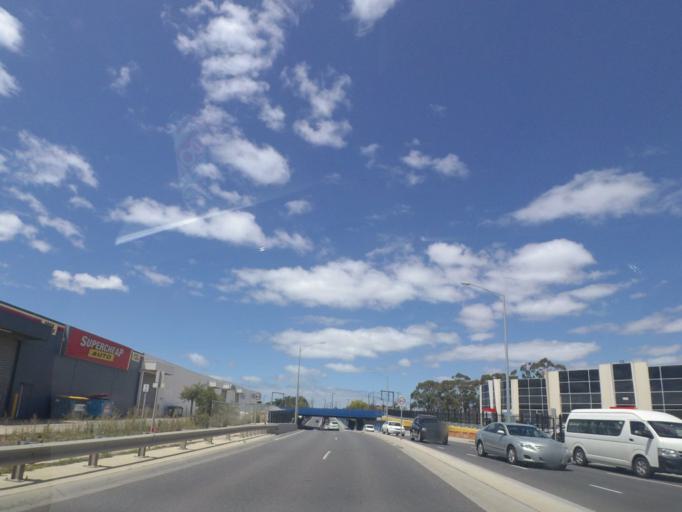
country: AU
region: Victoria
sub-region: Brimbank
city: Sunshine North
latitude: -37.7803
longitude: 144.8283
